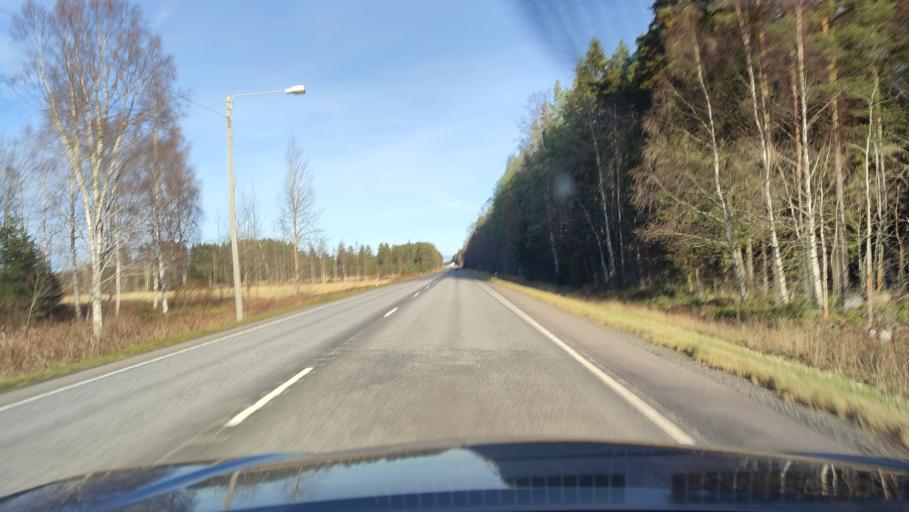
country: FI
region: Ostrobothnia
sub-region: Vaasa
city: Malax
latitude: 62.8089
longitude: 21.6813
